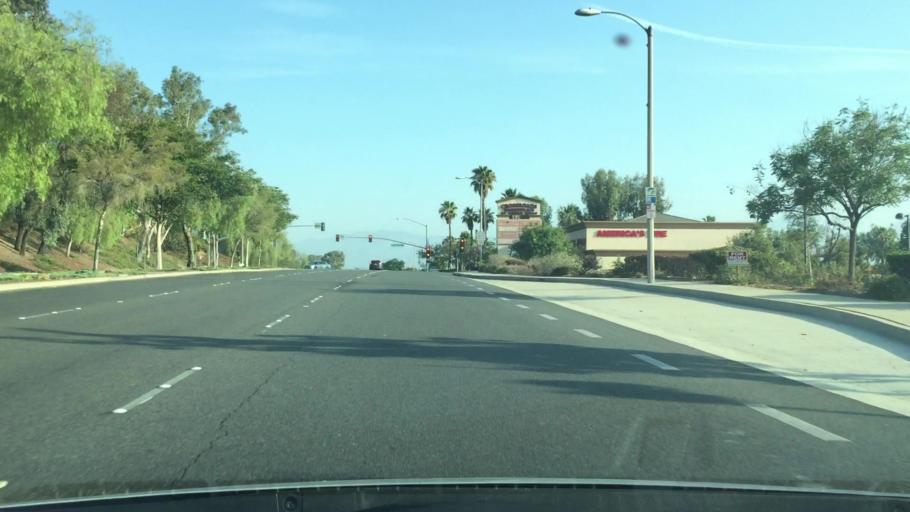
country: US
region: California
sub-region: San Bernardino County
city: Chino Hills
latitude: 34.0129
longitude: -117.7439
